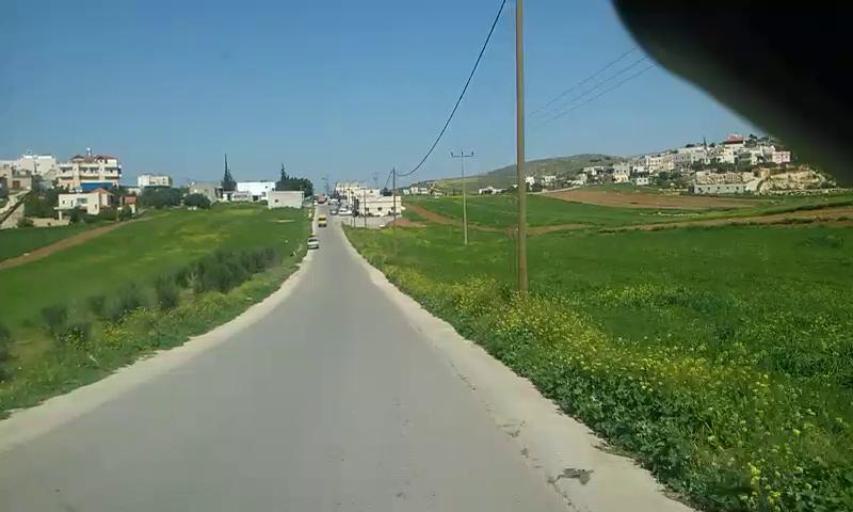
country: PS
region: West Bank
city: Al Majd
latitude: 31.4768
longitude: 34.9515
